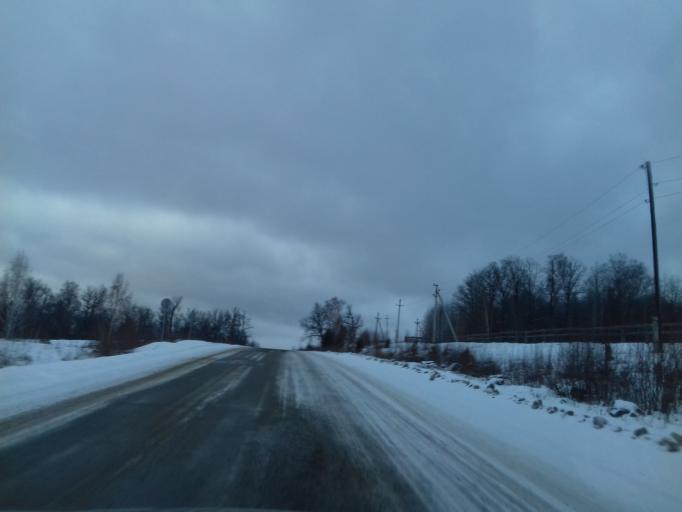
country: RU
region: Bashkortostan
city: Starosubkhangulovo
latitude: 53.2278
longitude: 57.4544
